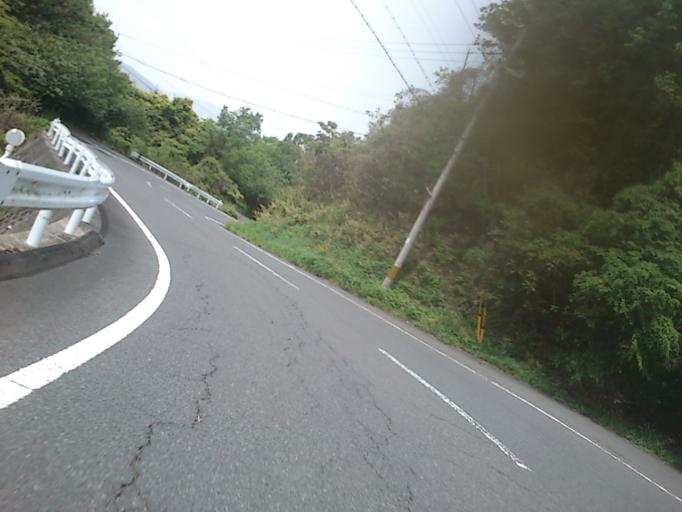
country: JP
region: Kyoto
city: Miyazu
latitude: 35.5877
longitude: 135.1192
